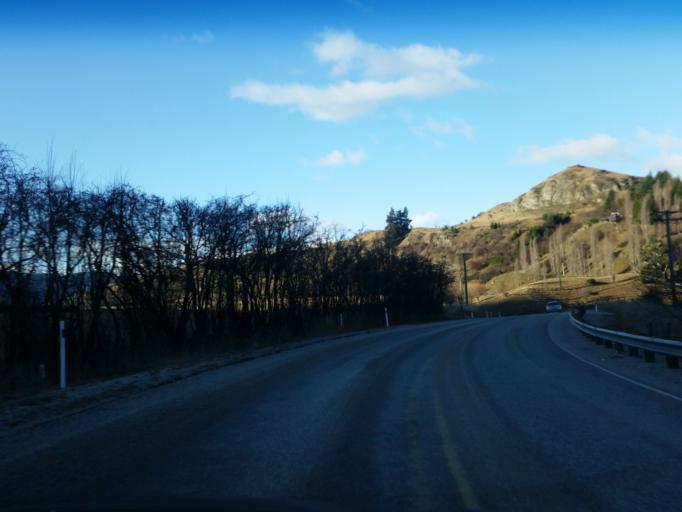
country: NZ
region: Otago
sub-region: Queenstown-Lakes District
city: Queenstown
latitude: -44.9705
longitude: 168.6989
